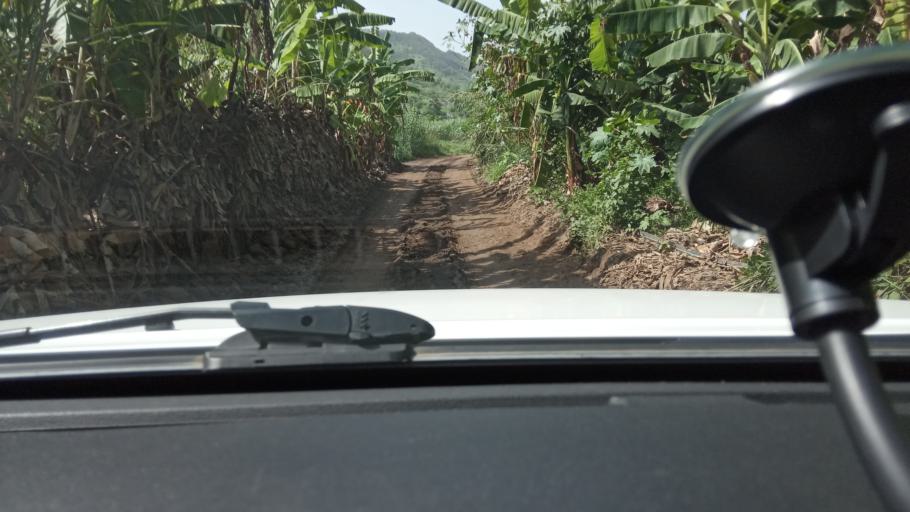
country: CV
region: Santa Cruz
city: Santa Cruz
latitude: 15.1151
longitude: -23.5504
